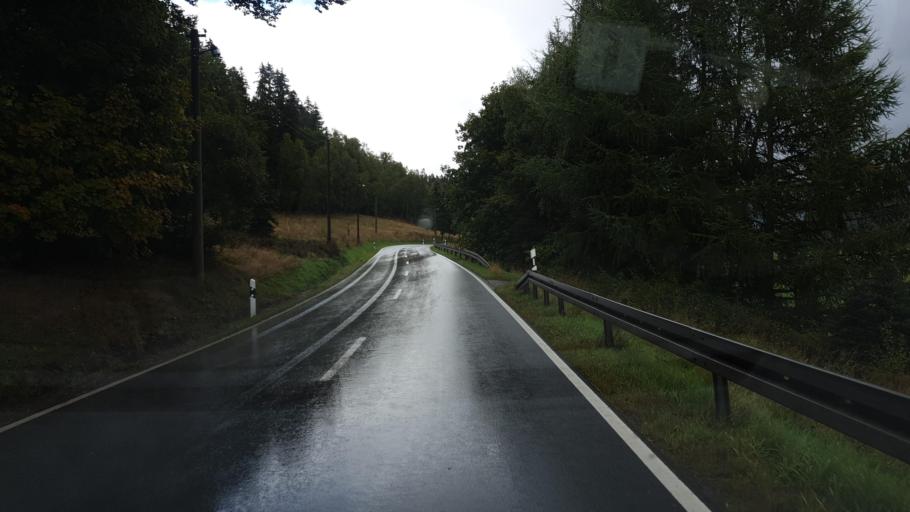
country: DE
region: Saxony
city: Neuhausen
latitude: 50.6873
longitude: 13.4780
